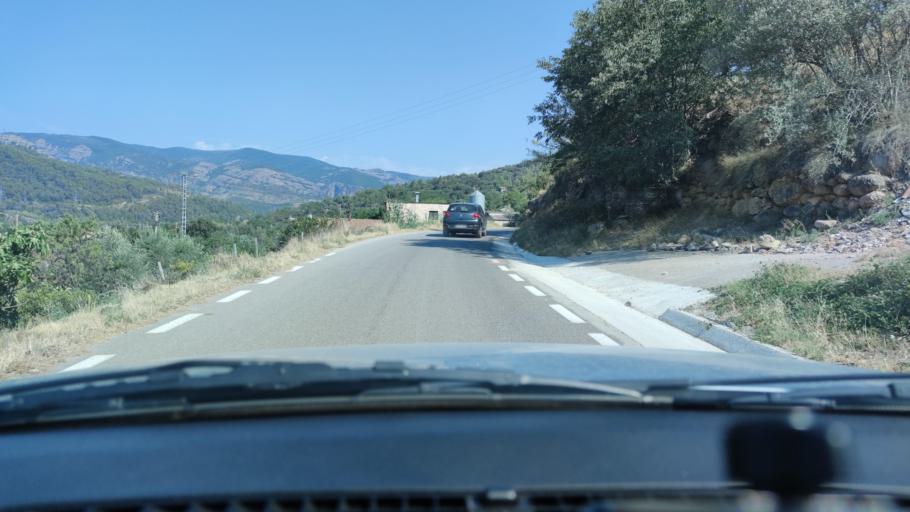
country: ES
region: Catalonia
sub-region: Provincia de Lleida
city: Senterada
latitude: 42.2567
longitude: 0.9630
